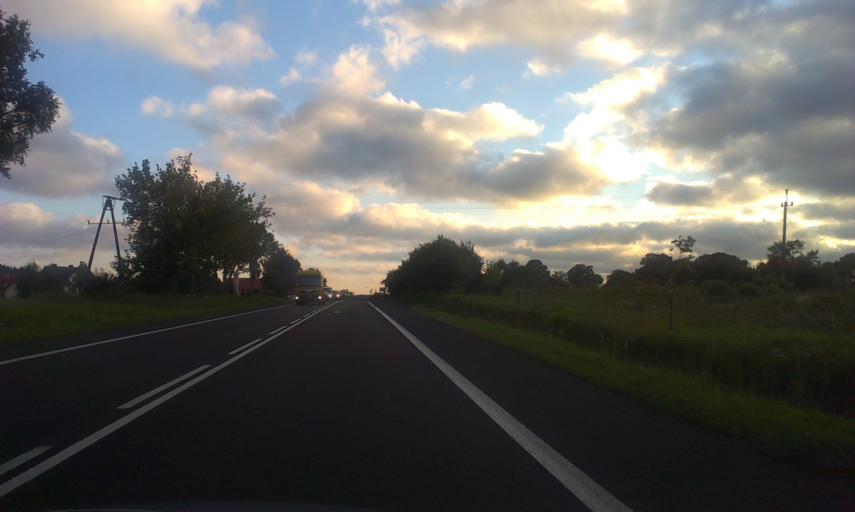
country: PL
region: West Pomeranian Voivodeship
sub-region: Powiat slawienski
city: Darlowo
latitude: 54.2751
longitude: 16.4319
